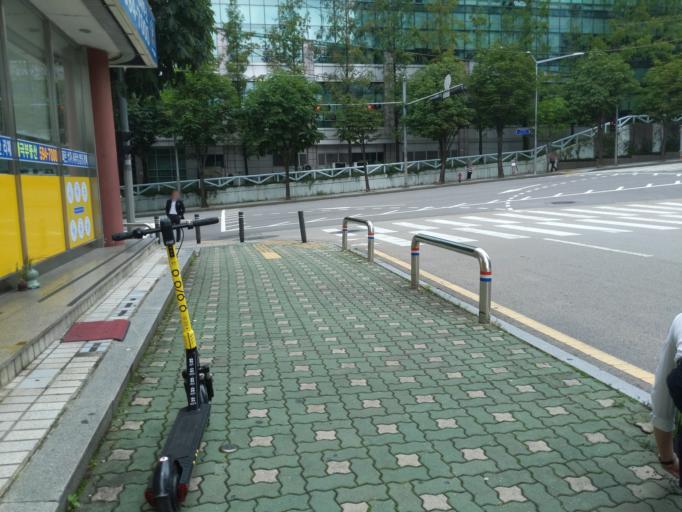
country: KR
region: Seoul
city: Seoul
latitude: 37.4969
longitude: 127.0134
